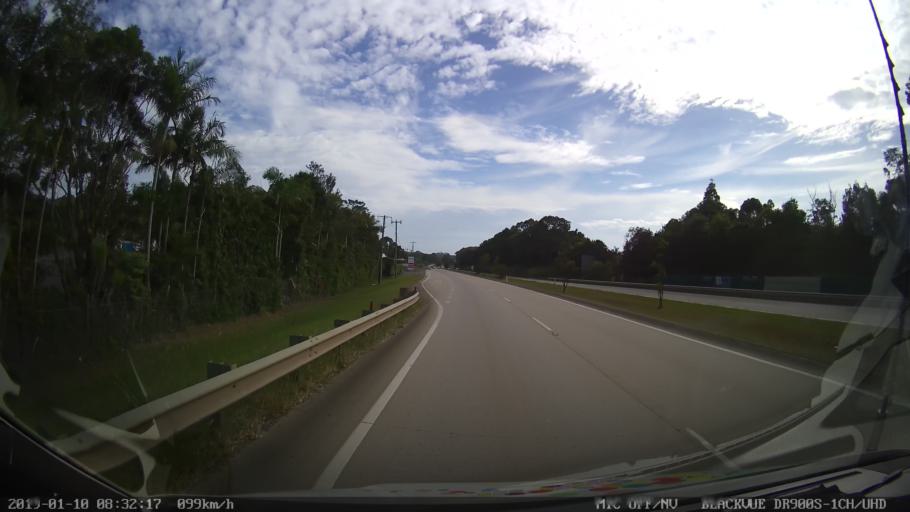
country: AU
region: New South Wales
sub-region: Coffs Harbour
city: Boambee
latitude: -30.3453
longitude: 153.0683
